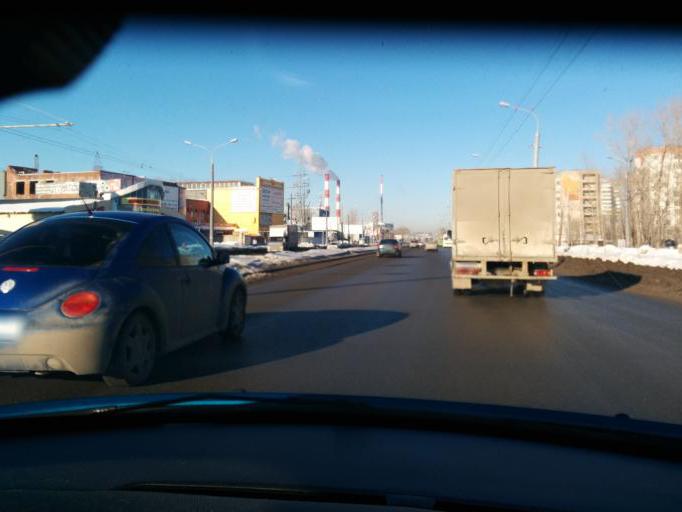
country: RU
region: Perm
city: Perm
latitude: 57.9681
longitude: 56.2620
